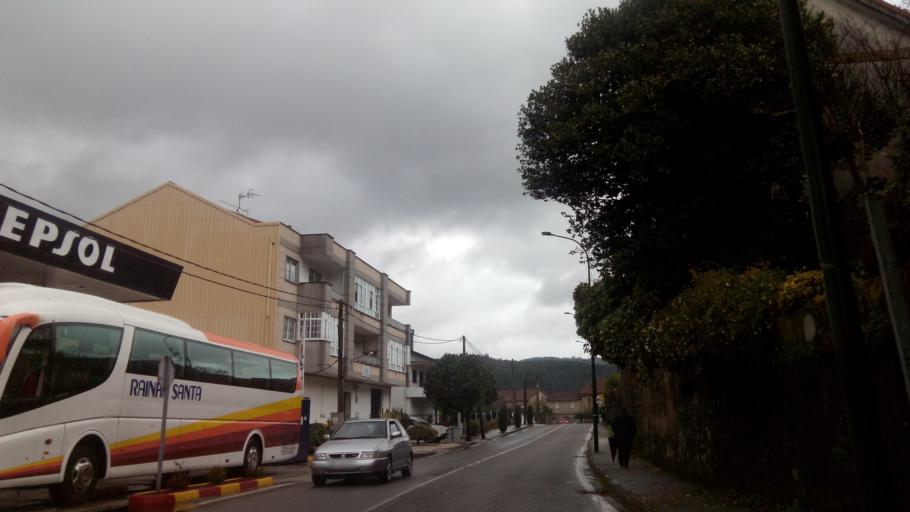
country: ES
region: Galicia
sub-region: Provincia de Pontevedra
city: Mondariz-Balneario
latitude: 42.2239
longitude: -8.4742
